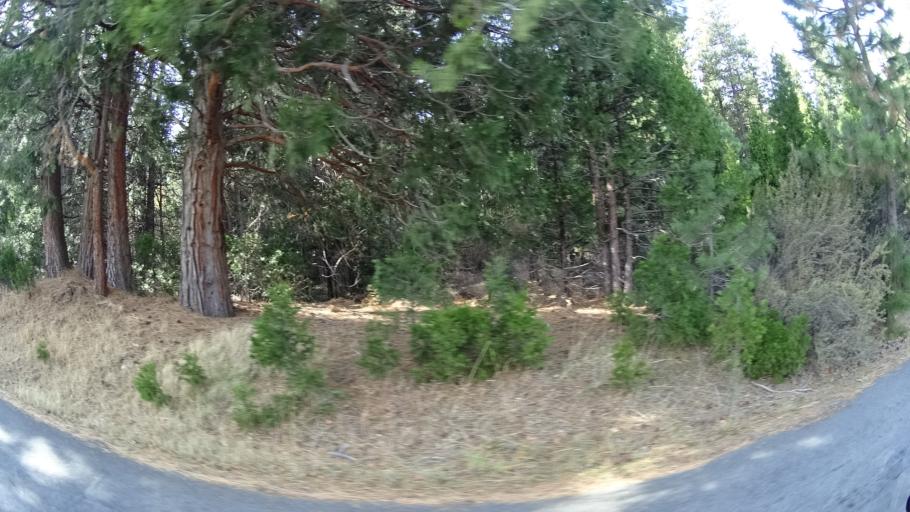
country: US
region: California
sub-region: Siskiyou County
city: Weed
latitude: 41.4281
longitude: -122.3974
